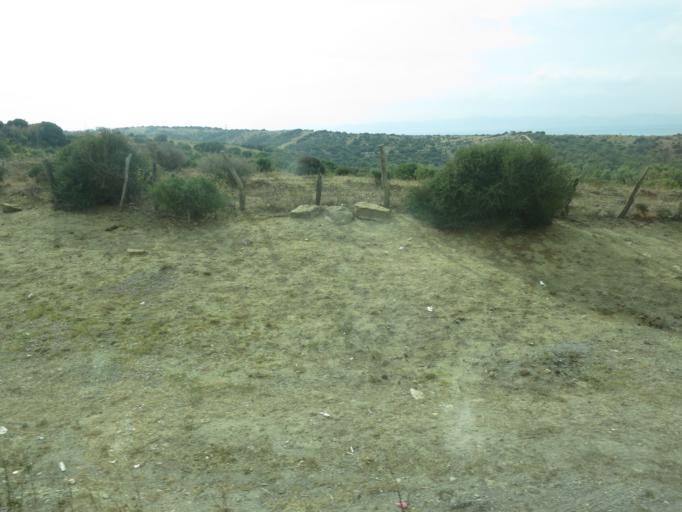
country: ES
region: Andalusia
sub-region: Provincia de Cadiz
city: Tarifa
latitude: 36.0223
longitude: -5.5973
